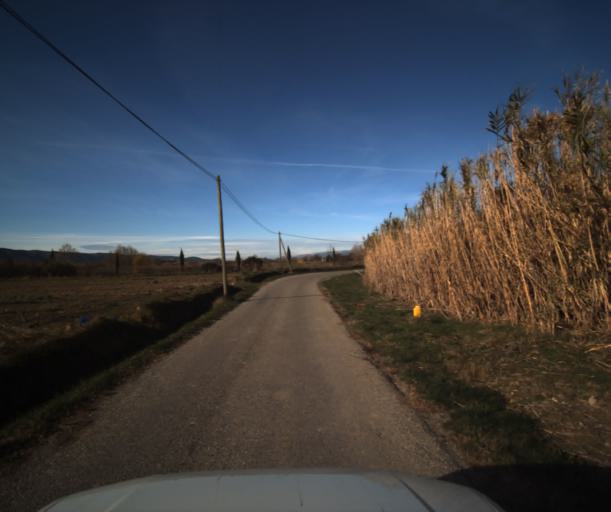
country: FR
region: Provence-Alpes-Cote d'Azur
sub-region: Departement du Vaucluse
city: Villelaure
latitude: 43.6957
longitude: 5.4473
